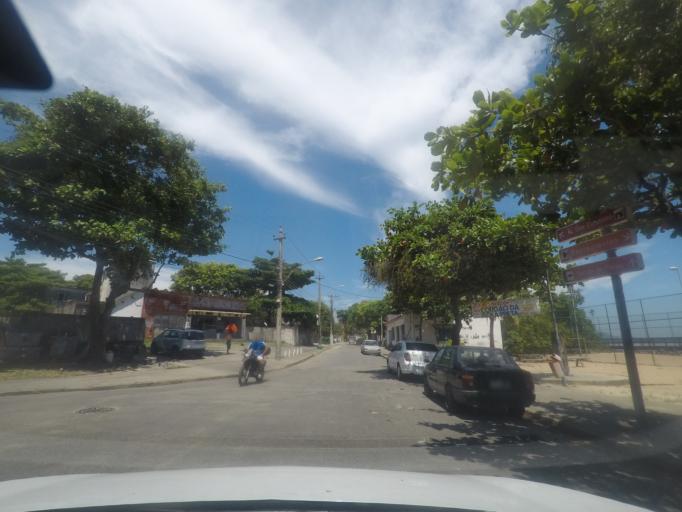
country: BR
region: Rio de Janeiro
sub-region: Itaguai
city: Itaguai
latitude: -23.0051
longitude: -43.6367
